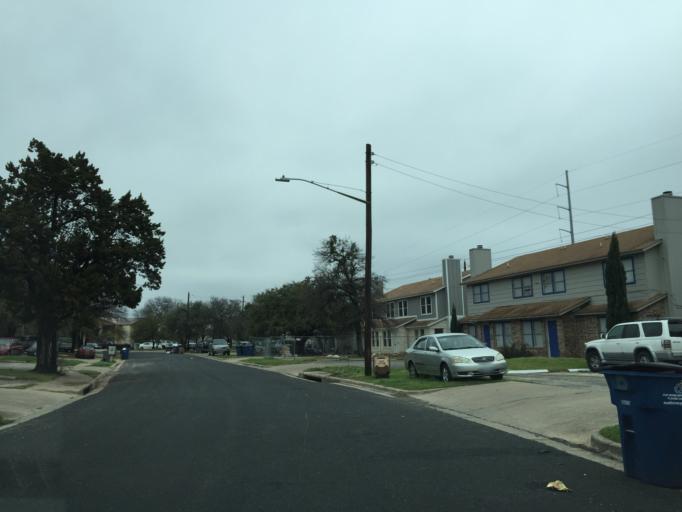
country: US
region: Texas
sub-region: Williamson County
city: Jollyville
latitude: 30.4131
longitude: -97.7299
